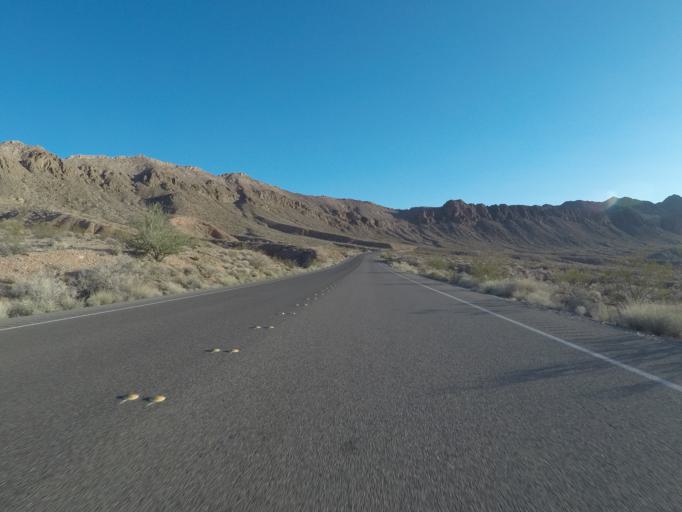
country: US
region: Nevada
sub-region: Clark County
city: Moapa Valley
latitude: 36.2587
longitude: -114.4827
